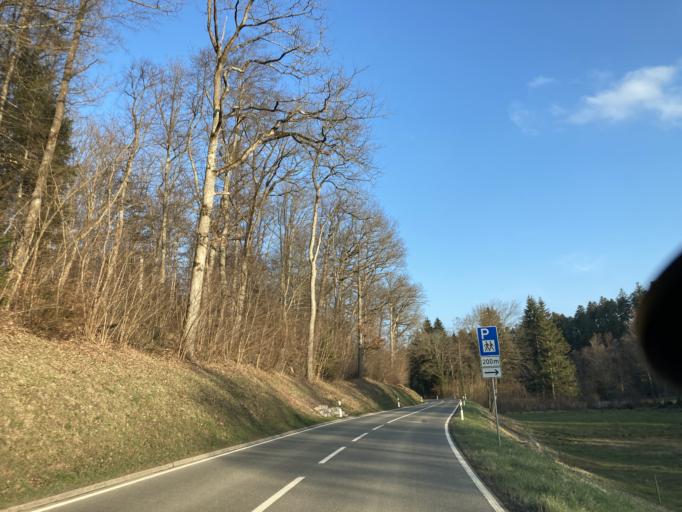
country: DE
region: Baden-Wuerttemberg
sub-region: Tuebingen Region
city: Bodelshausen
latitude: 48.4264
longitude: 8.9742
